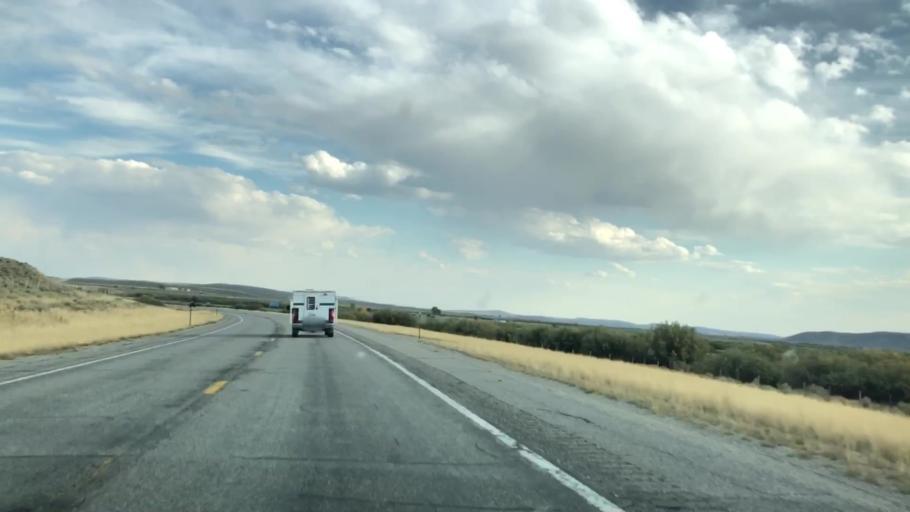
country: US
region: Wyoming
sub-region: Sublette County
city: Pinedale
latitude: 43.0229
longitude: -110.1230
